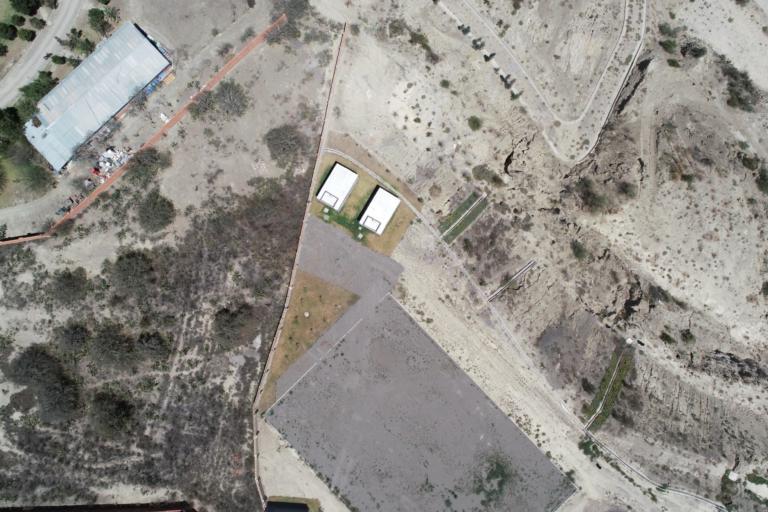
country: BO
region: La Paz
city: La Paz
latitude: -16.6212
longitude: -68.0588
